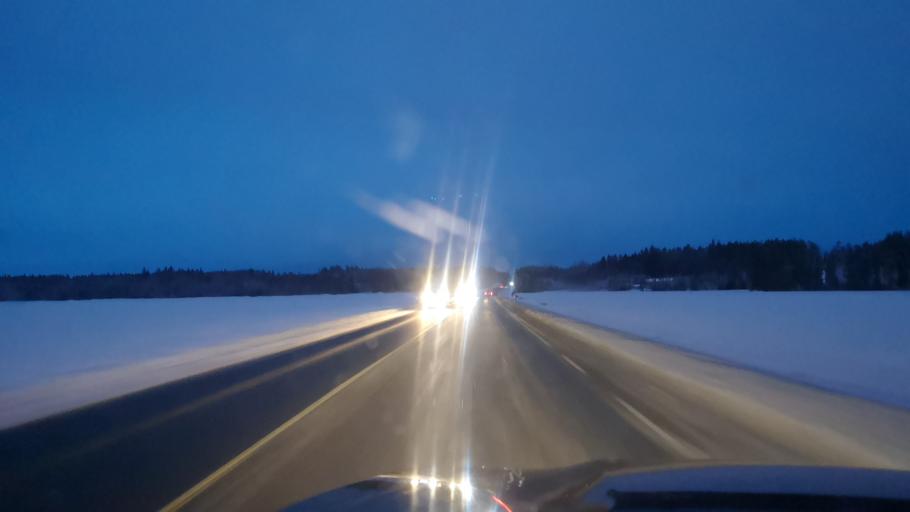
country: FI
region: Varsinais-Suomi
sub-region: Loimaa
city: Loimaa
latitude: 60.8632
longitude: 23.0501
